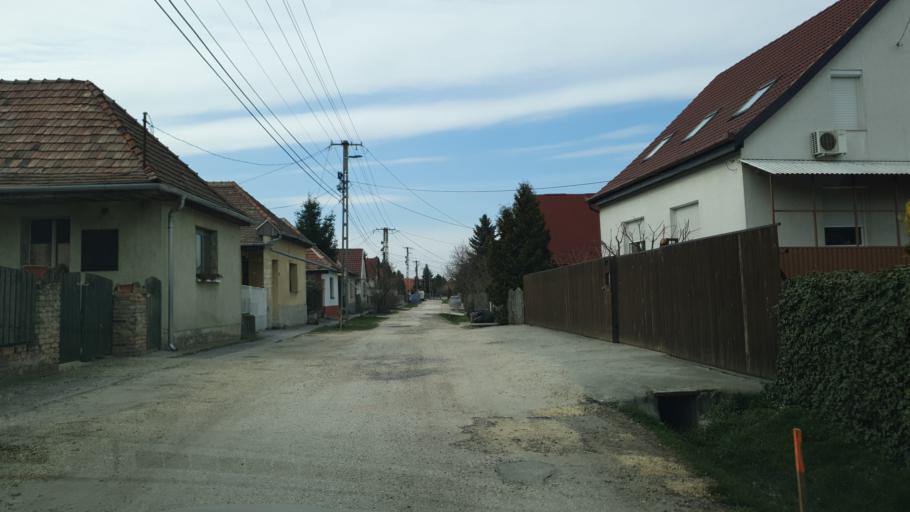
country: HU
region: Fejer
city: Etyek
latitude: 47.4423
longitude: 18.7574
